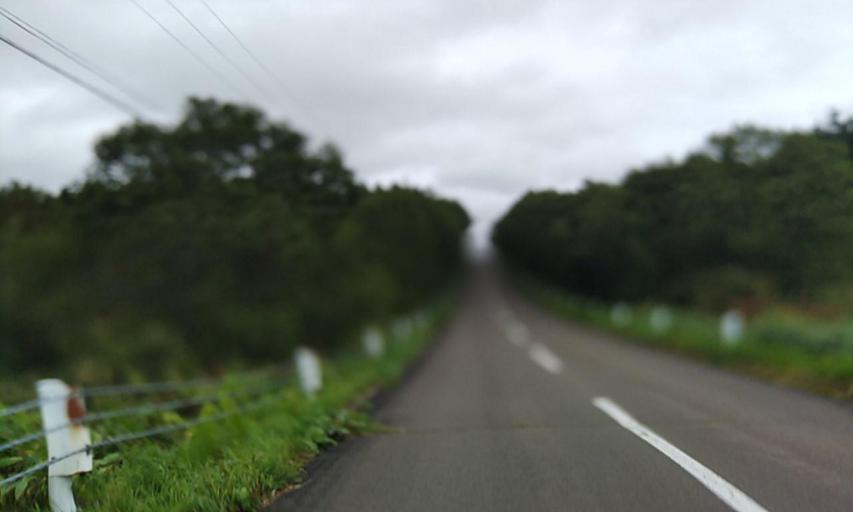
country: JP
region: Hokkaido
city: Nemuro
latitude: 43.2687
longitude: 145.2655
